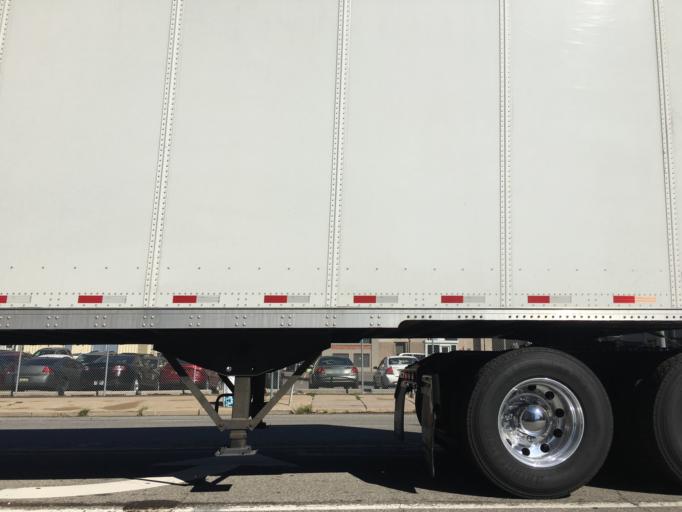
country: US
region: Michigan
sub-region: Wayne County
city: Detroit
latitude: 42.3275
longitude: -83.0546
